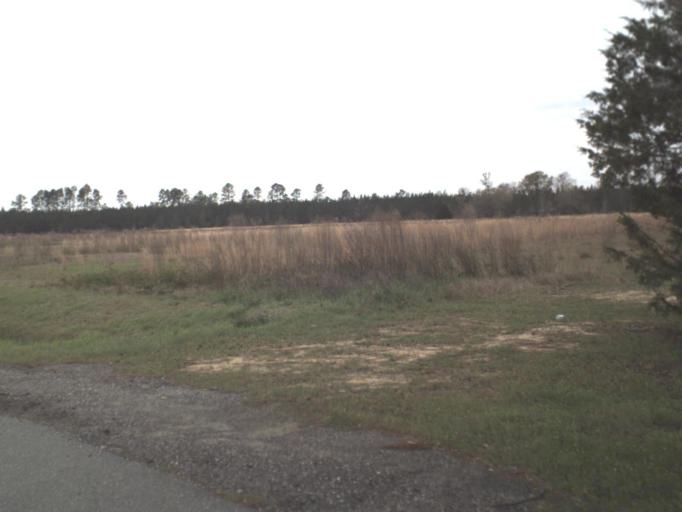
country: US
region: Florida
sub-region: Calhoun County
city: Blountstown
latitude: 30.3352
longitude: -85.2202
